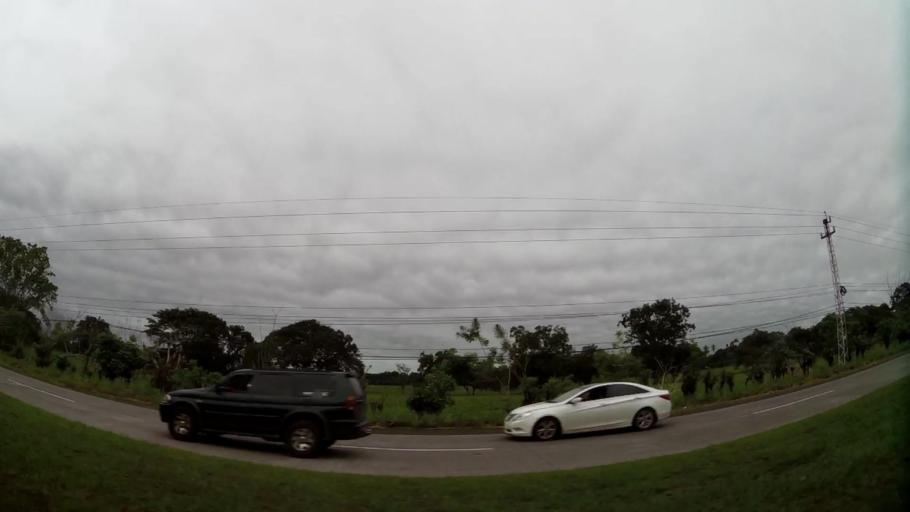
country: PA
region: Chiriqui
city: Tijera
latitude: 8.4801
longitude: -82.5559
